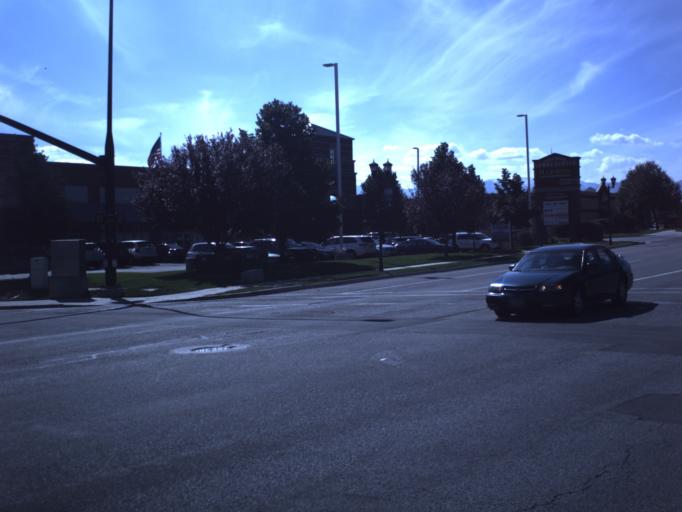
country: US
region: Utah
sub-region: Salt Lake County
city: South Jordan
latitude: 40.5624
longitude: -111.9359
